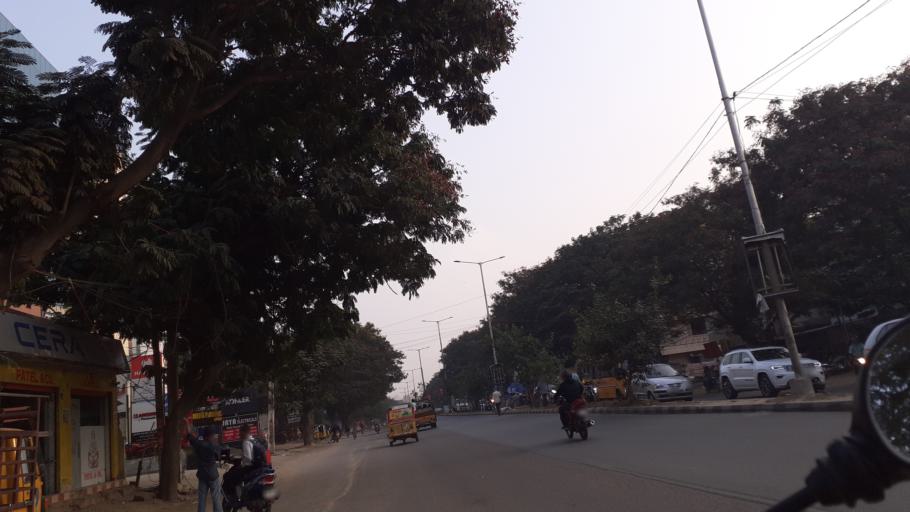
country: IN
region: Telangana
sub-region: Rangareddi
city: Kukatpalli
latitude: 17.4745
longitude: 78.3638
